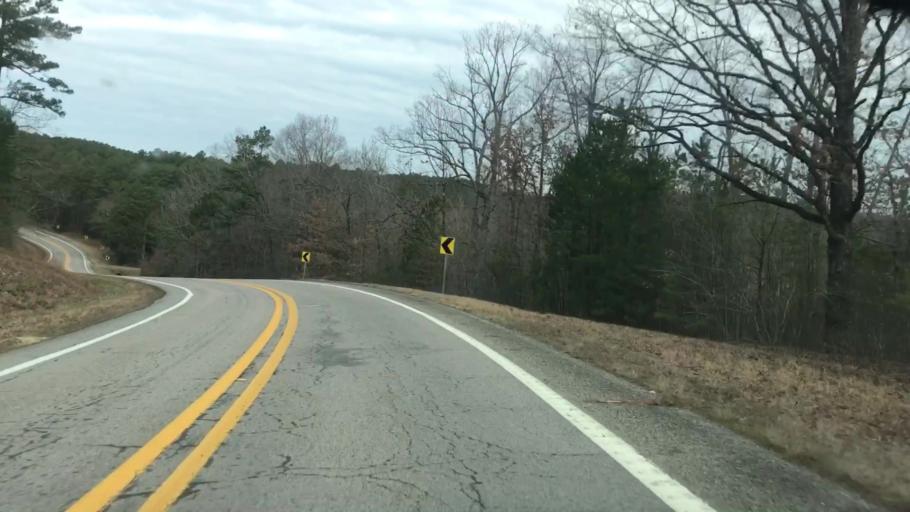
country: US
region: Arkansas
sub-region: Montgomery County
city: Mount Ida
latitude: 34.6689
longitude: -93.7757
